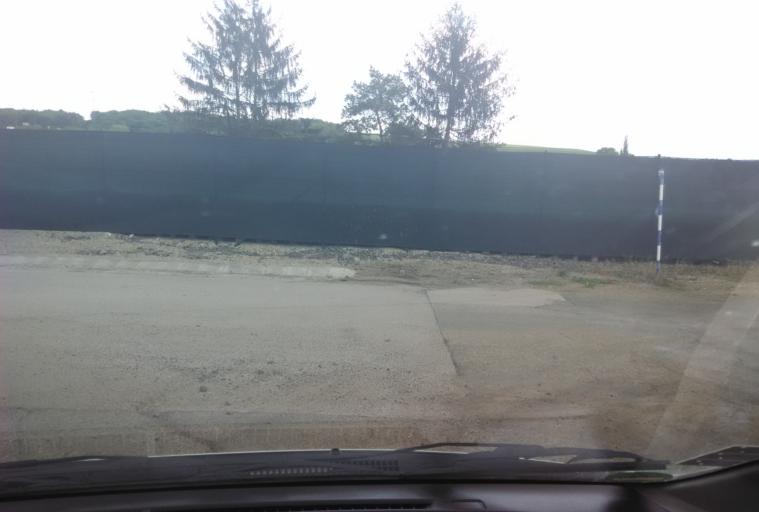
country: SK
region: Nitriansky
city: Levice
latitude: 48.1974
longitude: 18.6574
